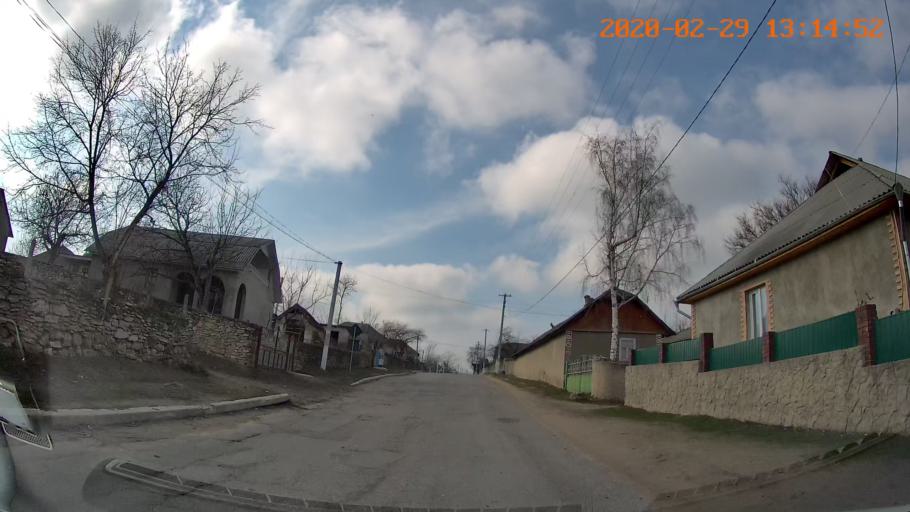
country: MD
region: Telenesti
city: Camenca
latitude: 48.0114
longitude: 28.6743
